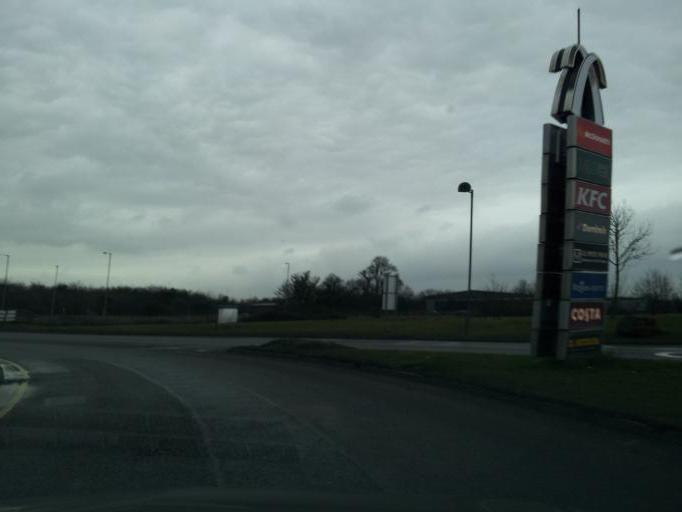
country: GB
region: England
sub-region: Cambridgeshire
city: Swavesey
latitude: 52.2706
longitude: -0.0106
